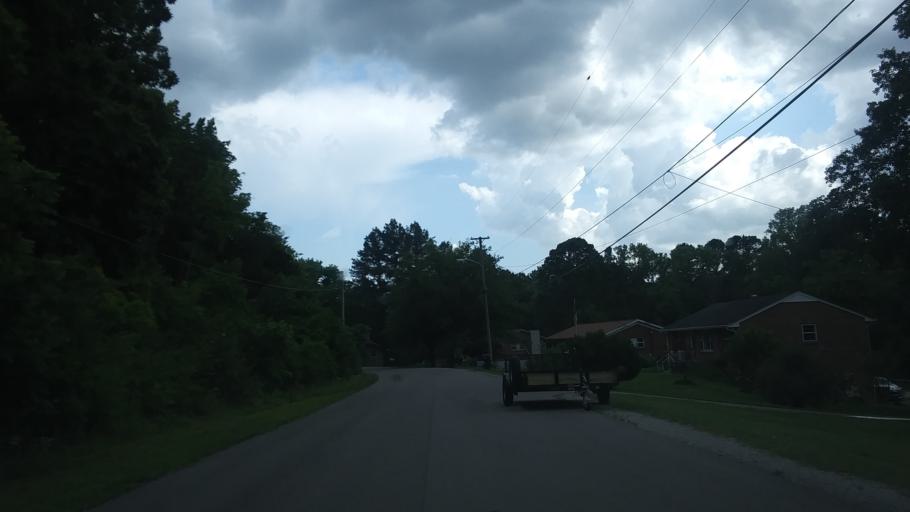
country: US
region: Tennessee
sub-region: Davidson County
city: Oak Hill
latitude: 36.0755
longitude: -86.6989
